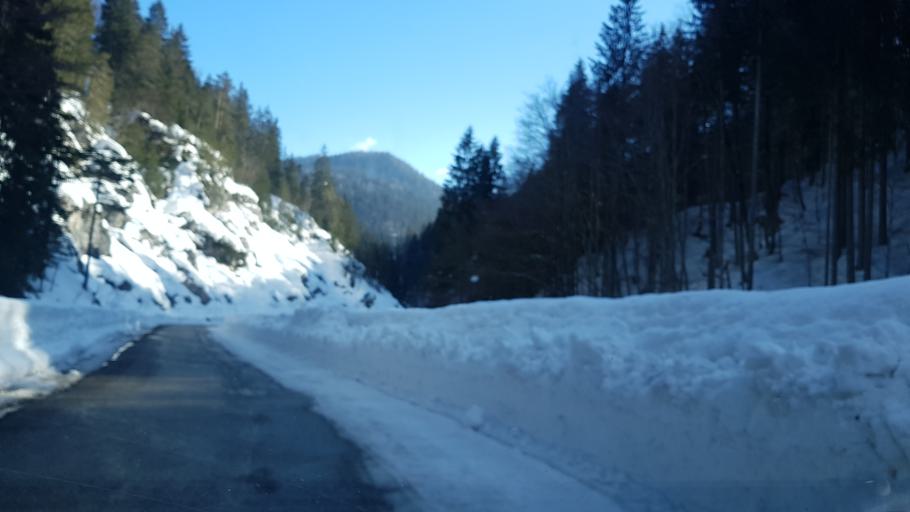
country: IT
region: Friuli Venezia Giulia
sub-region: Provincia di Udine
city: Malborghetto
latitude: 46.5313
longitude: 13.4707
